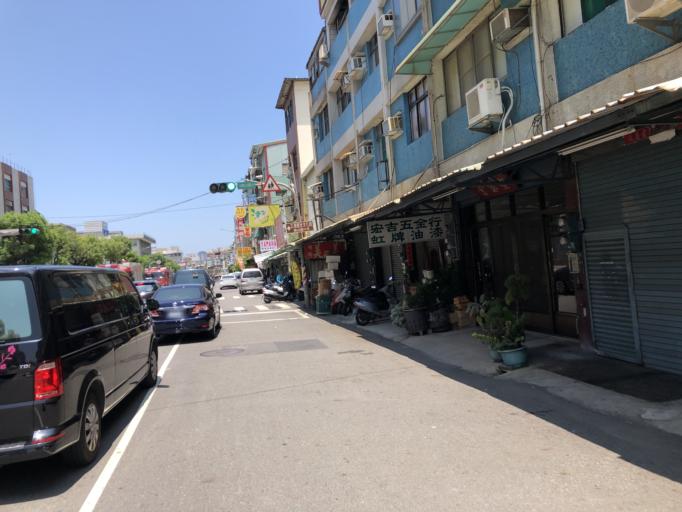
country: TW
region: Kaohsiung
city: Kaohsiung
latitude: 22.6306
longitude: 120.2811
